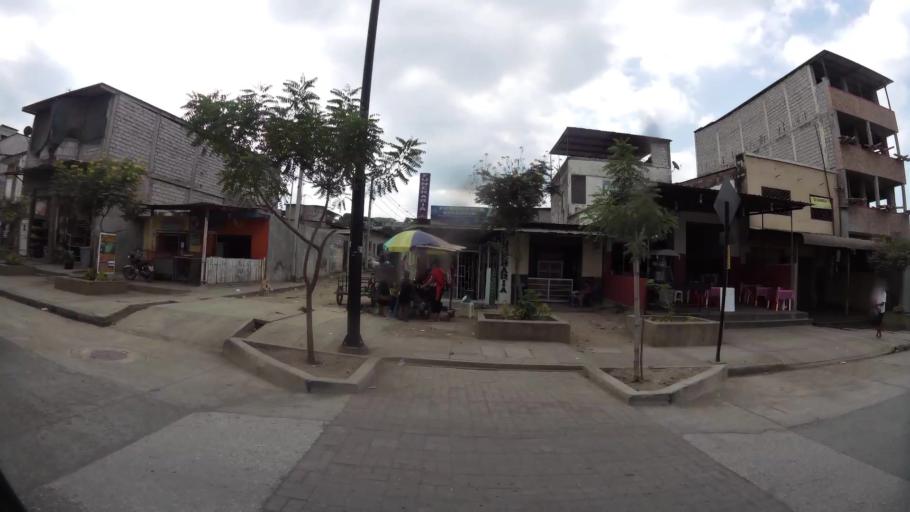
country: EC
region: Guayas
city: Santa Lucia
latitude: -2.1031
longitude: -79.9493
